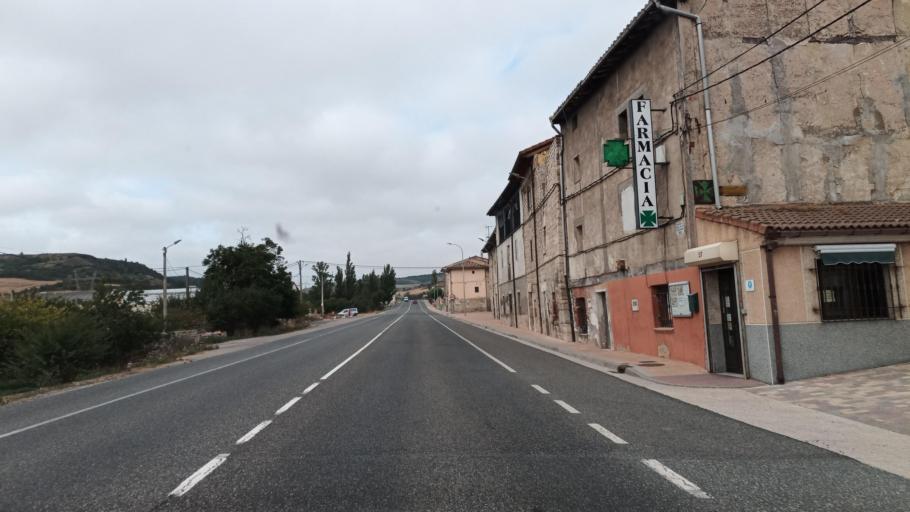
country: ES
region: Castille and Leon
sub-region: Provincia de Burgos
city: Monasterio de Rodilla
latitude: 42.4580
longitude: -3.4654
